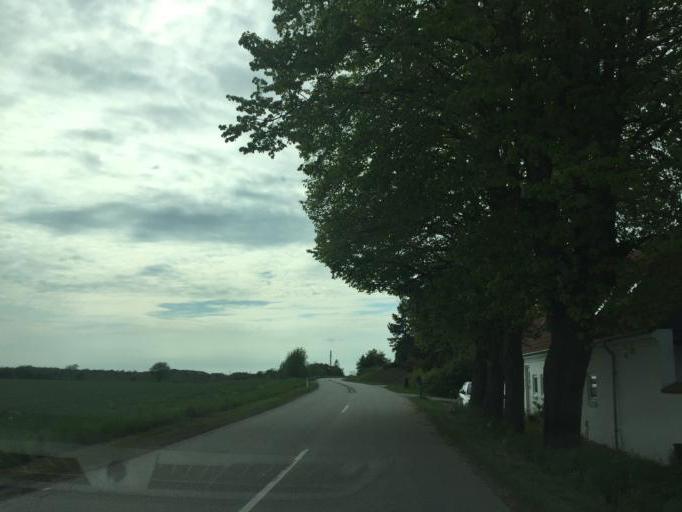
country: DK
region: South Denmark
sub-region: Odense Kommune
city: Hojby
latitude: 55.3403
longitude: 10.4590
